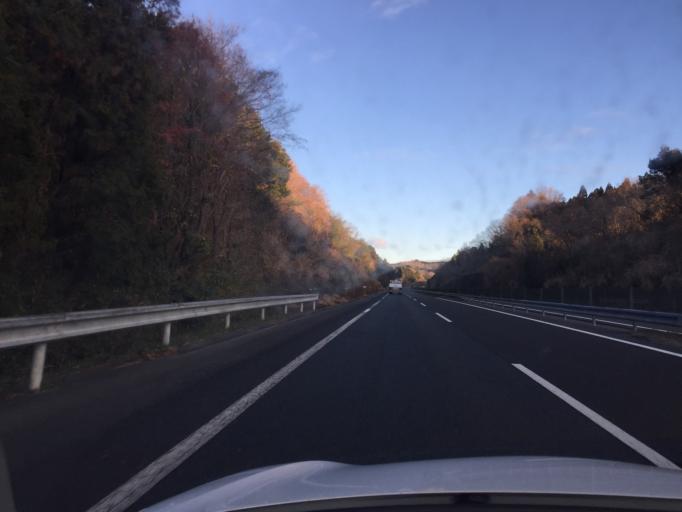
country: JP
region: Ibaraki
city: Kitaibaraki
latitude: 36.8165
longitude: 140.7305
